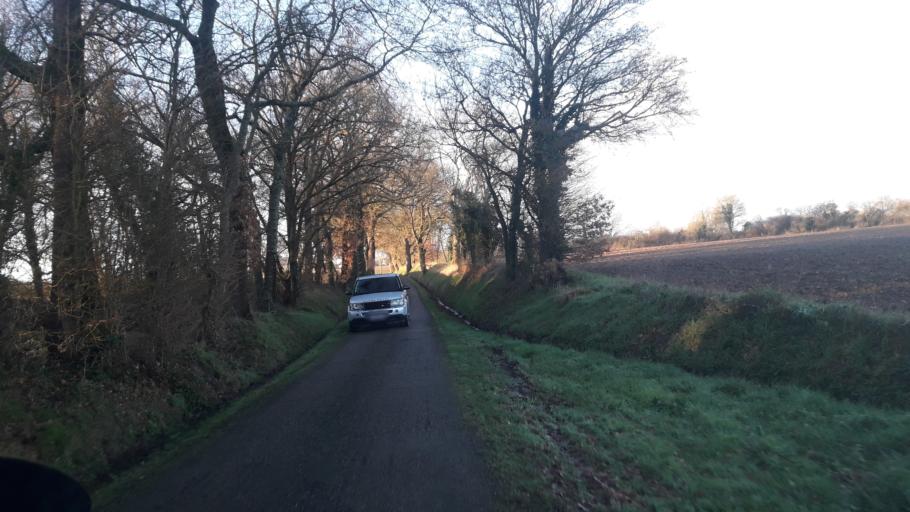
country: FR
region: Midi-Pyrenees
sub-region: Departement du Gers
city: Gimont
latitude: 43.7156
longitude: 0.9593
